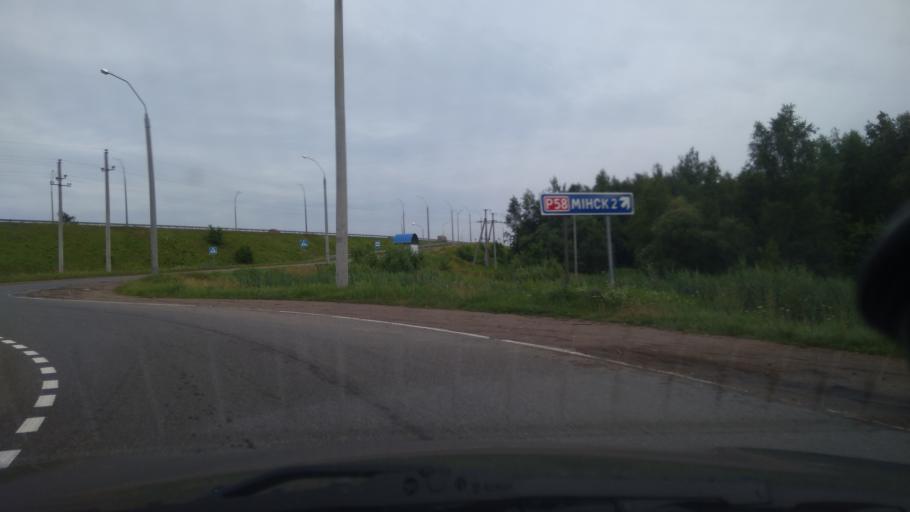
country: BY
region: Minsk
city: Bal'shavik
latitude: 53.9855
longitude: 27.5302
